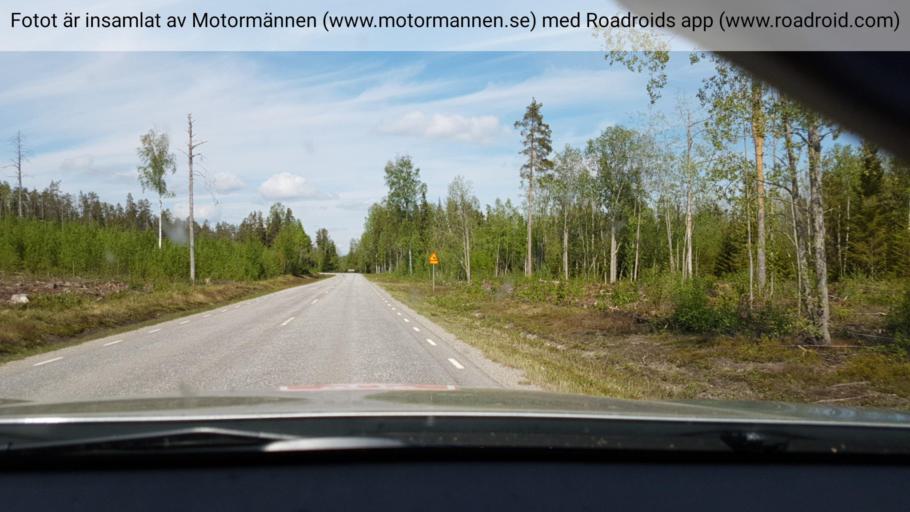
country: SE
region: Vaesterbotten
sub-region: Umea Kommun
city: Roback
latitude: 63.8481
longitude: 20.0902
